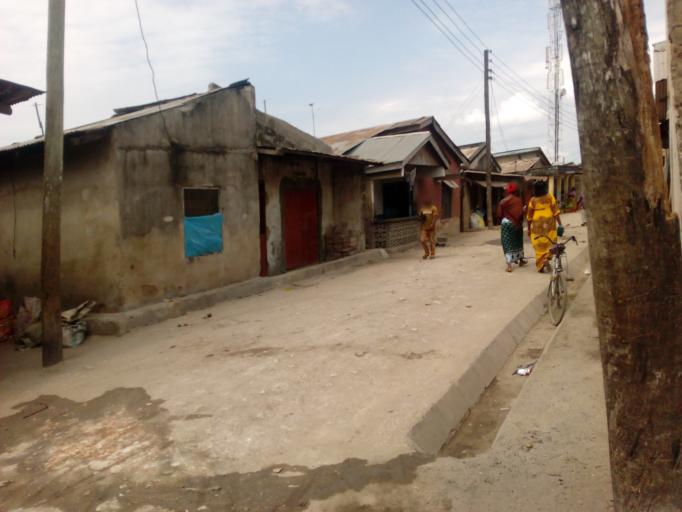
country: TZ
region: Dar es Salaam
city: Dar es Salaam
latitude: -6.8582
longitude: 39.2551
